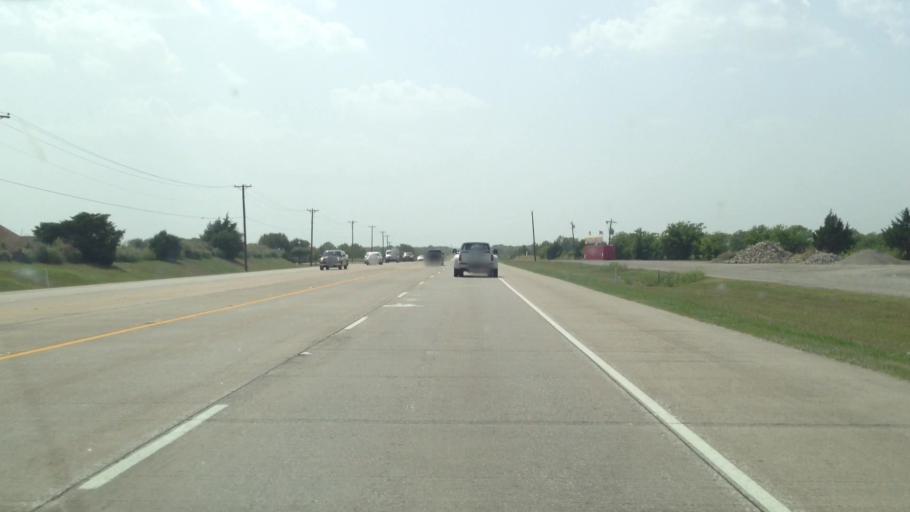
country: US
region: Texas
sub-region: Collin County
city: Princeton
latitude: 33.1677
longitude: -96.4617
